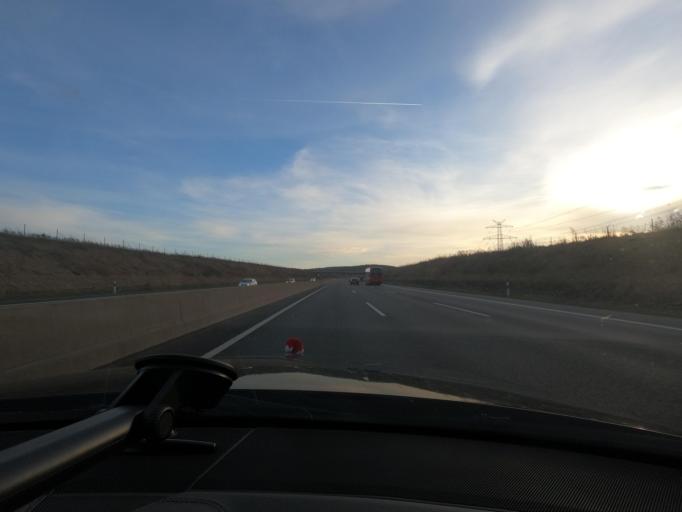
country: DE
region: Lower Saxony
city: Haverlah
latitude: 52.0739
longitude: 10.1925
